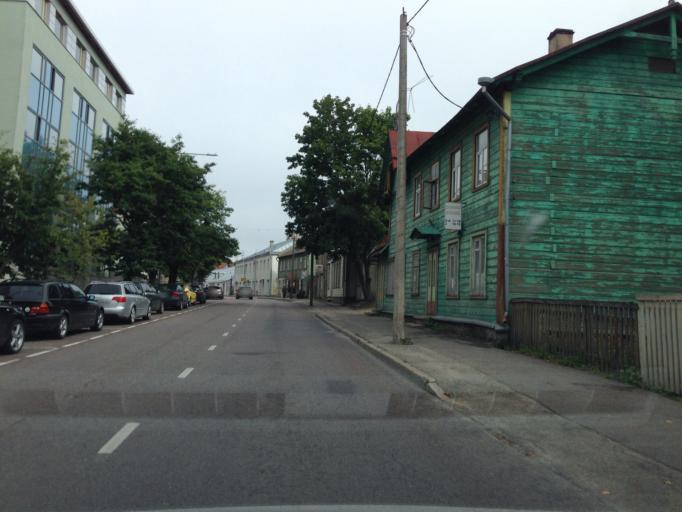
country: EE
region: Tartu
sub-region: Tartu linn
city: Tartu
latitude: 58.3723
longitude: 26.7225
